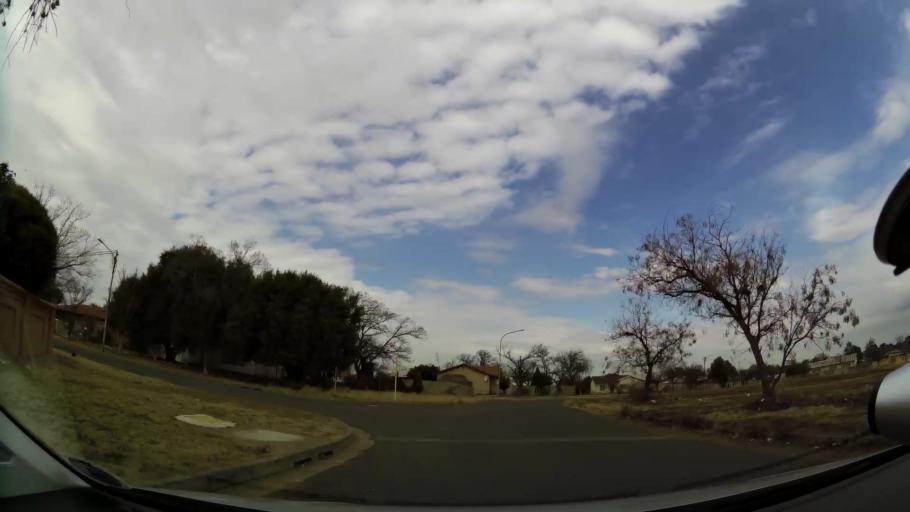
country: ZA
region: Orange Free State
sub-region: Fezile Dabi District Municipality
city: Kroonstad
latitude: -27.6423
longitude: 27.2290
